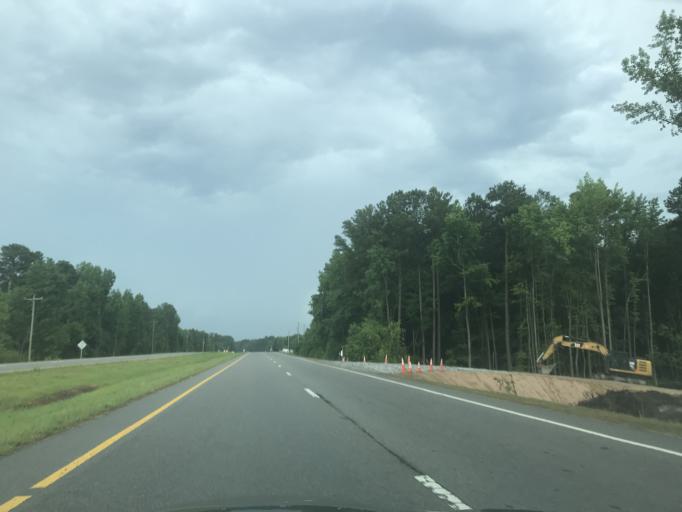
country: US
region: North Carolina
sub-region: Johnston County
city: Wilsons Mills
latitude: 35.5842
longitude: -78.4031
